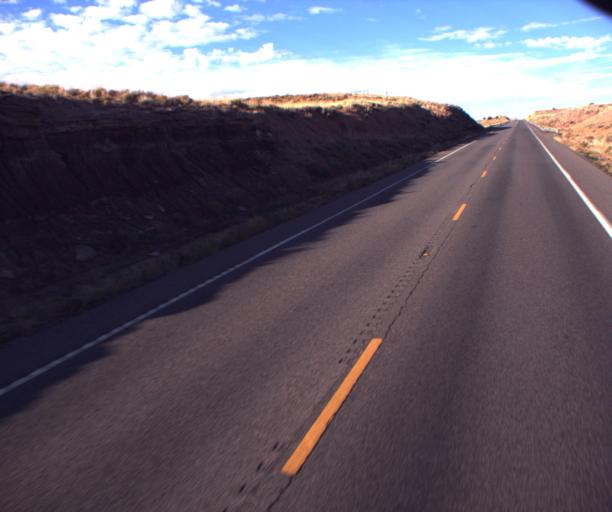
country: US
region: New Mexico
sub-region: San Juan County
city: Shiprock
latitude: 36.9358
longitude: -109.1257
